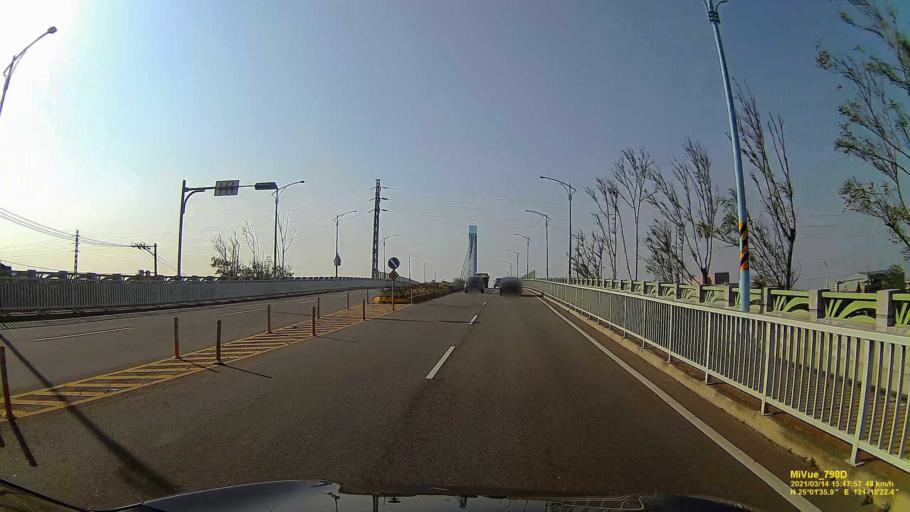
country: TW
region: Taiwan
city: Taoyuan City
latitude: 25.0270
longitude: 121.2559
